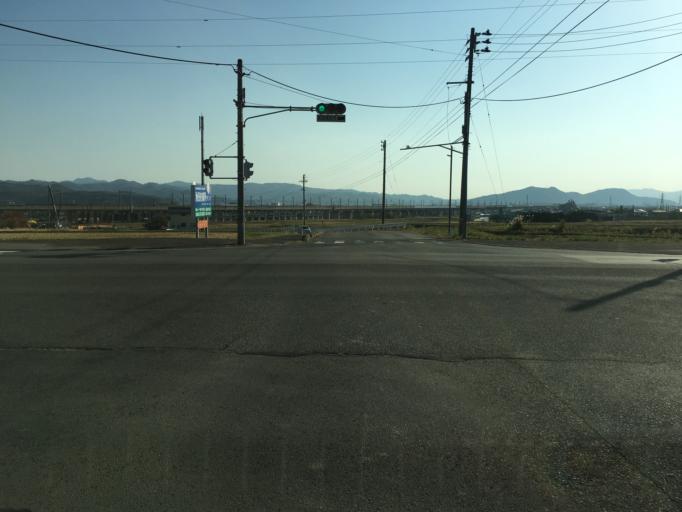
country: JP
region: Fukushima
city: Hobaramachi
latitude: 37.8351
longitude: 140.4973
